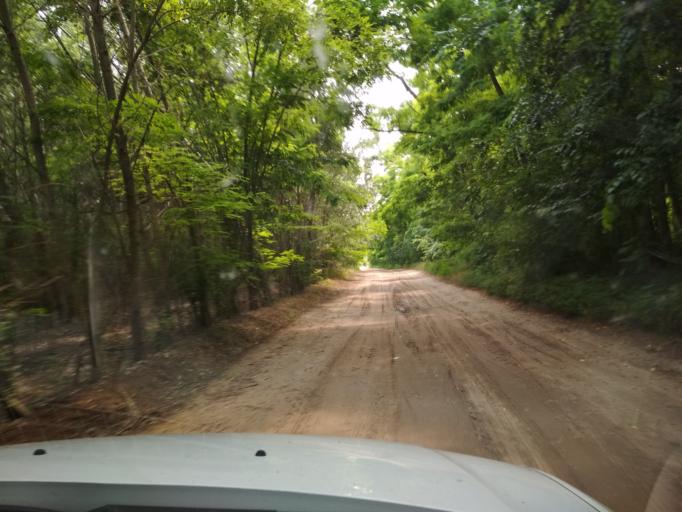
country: HU
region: Pest
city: Tapioszentmarton
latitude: 47.3540
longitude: 19.7462
